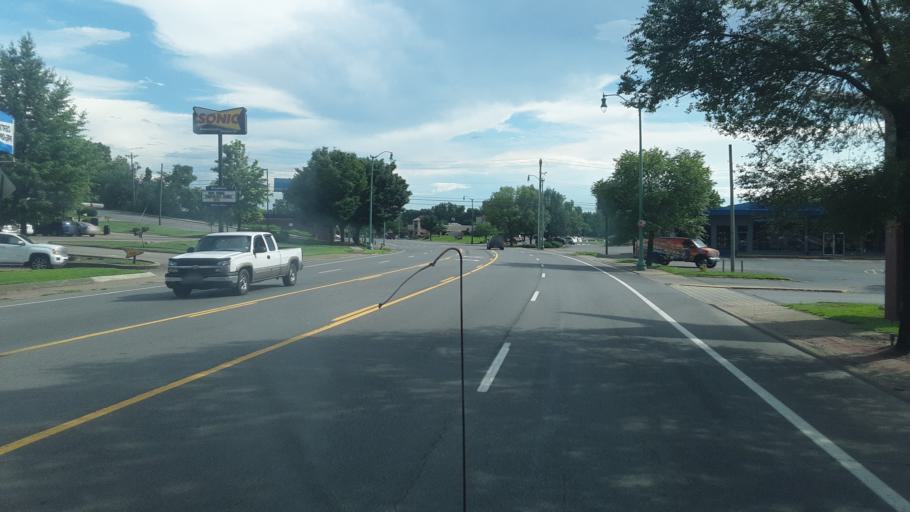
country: US
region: Tennessee
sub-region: Montgomery County
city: Clarksville
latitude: 36.5386
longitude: -87.3670
